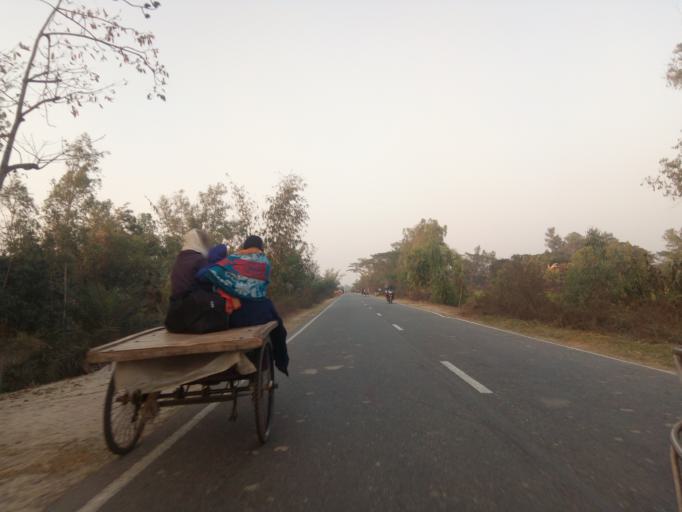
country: BD
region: Rajshahi
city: Bogra
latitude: 24.6048
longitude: 89.2399
